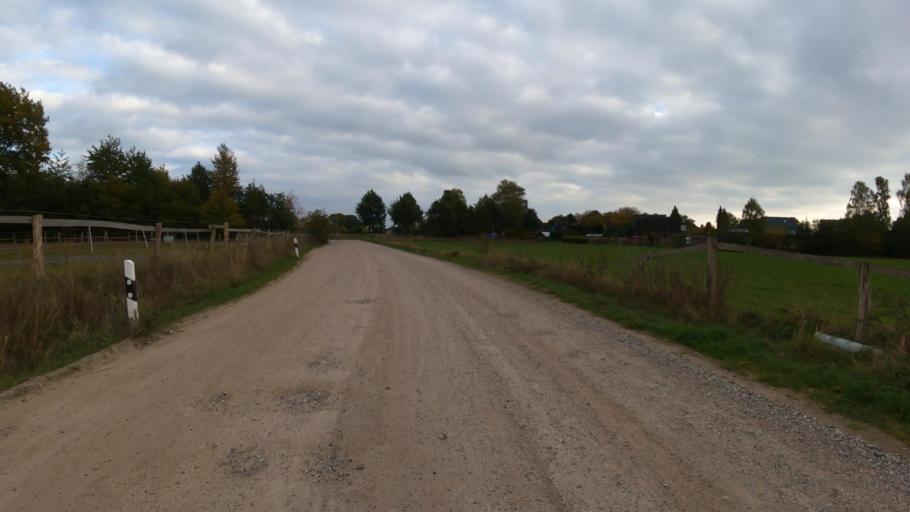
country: DE
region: Schleswig-Holstein
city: Ahrensburg
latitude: 53.6483
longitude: 10.2433
